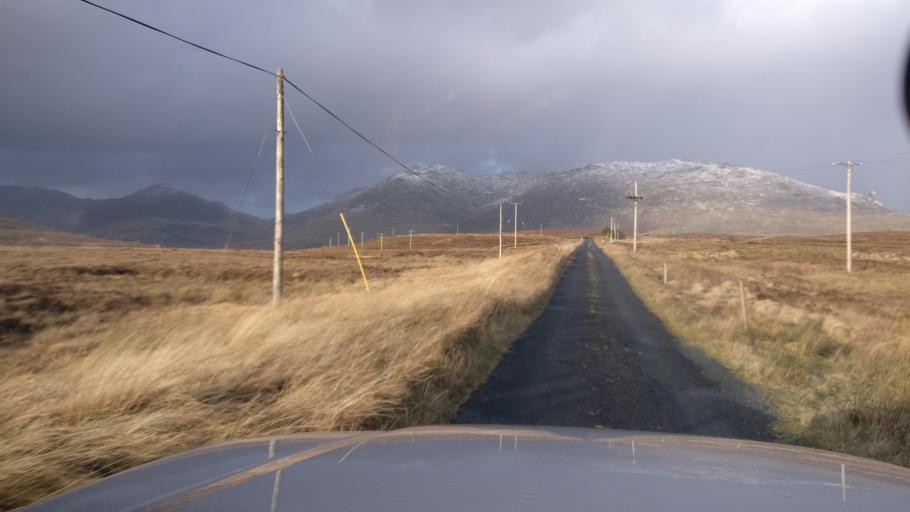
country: IE
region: Connaught
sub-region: County Galway
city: Clifden
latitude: 53.4696
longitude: -9.6936
